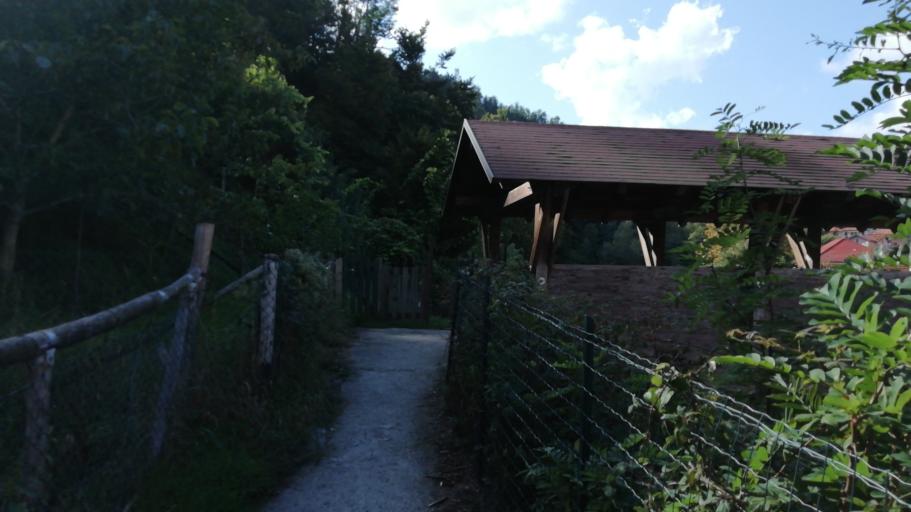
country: IT
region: Liguria
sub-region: Provincia di Genova
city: Masone
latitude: 44.5010
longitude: 8.7148
